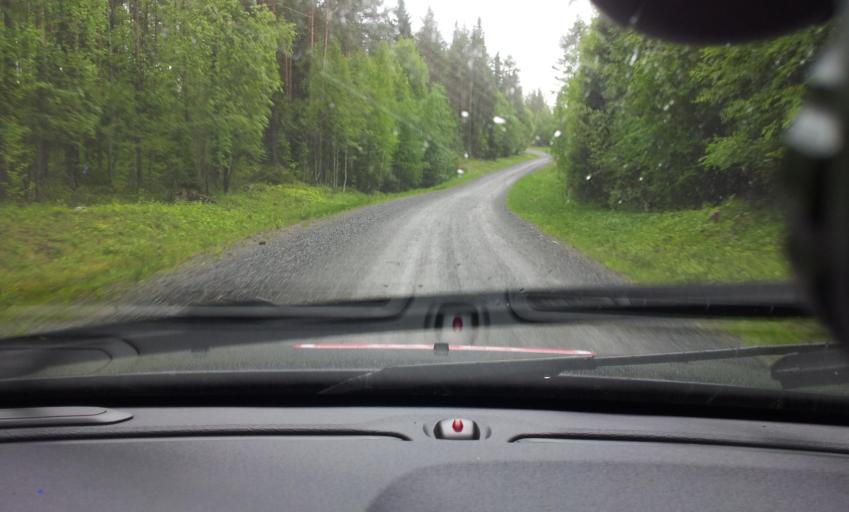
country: SE
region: Jaemtland
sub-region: OEstersunds Kommun
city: Brunflo
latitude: 63.1074
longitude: 15.0933
